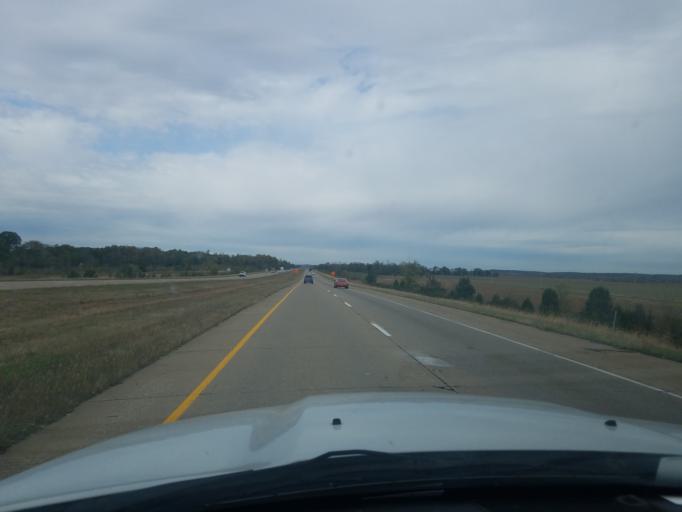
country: US
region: Indiana
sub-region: Vanderburgh County
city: Melody Hill
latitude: 38.0503
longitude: -87.4745
